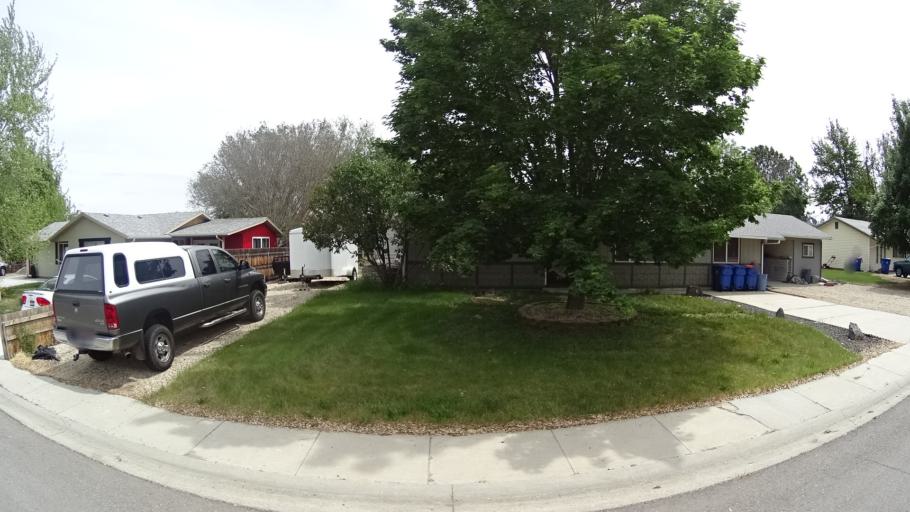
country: US
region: Idaho
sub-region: Ada County
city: Meridian
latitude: 43.5404
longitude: -116.3251
